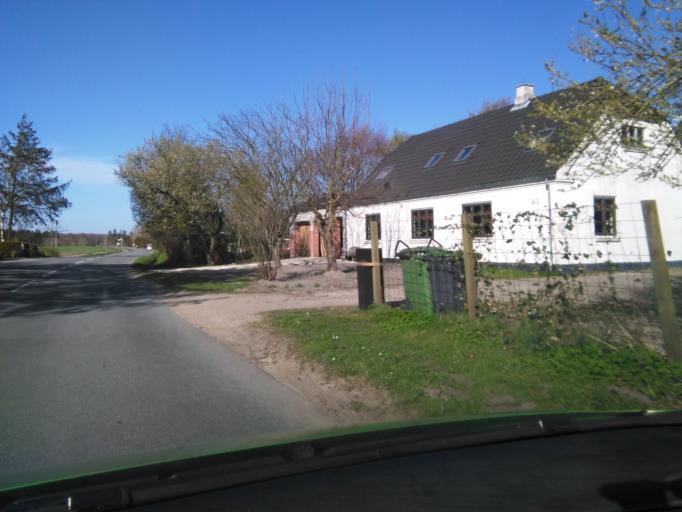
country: DK
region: South Denmark
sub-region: Varde Kommune
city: Oksbol
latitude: 55.6426
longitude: 8.2827
